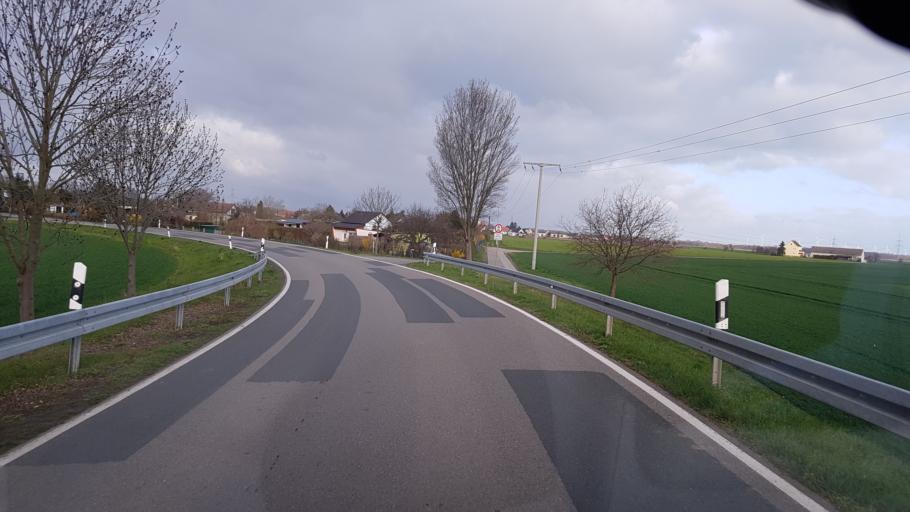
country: DE
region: Saxony
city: Nauwalde
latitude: 51.4193
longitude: 13.4215
